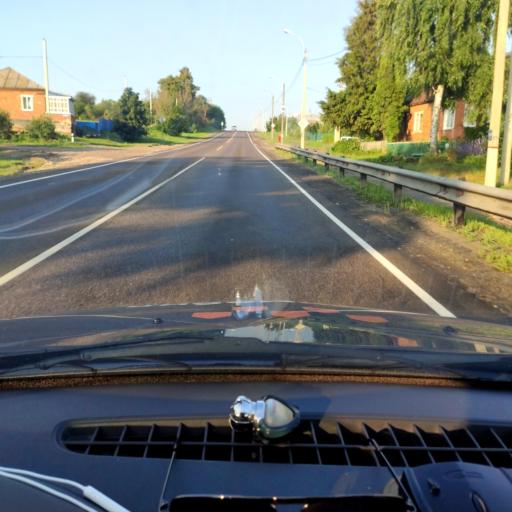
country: RU
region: Lipetsk
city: Kazaki
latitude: 52.6225
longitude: 38.2709
